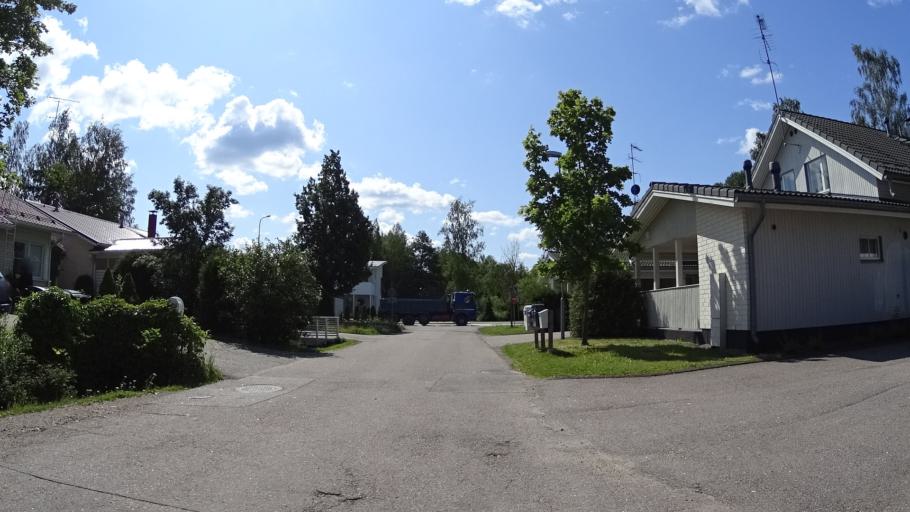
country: FI
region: Uusimaa
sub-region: Helsinki
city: Jaervenpaeae
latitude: 60.4716
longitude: 25.0784
